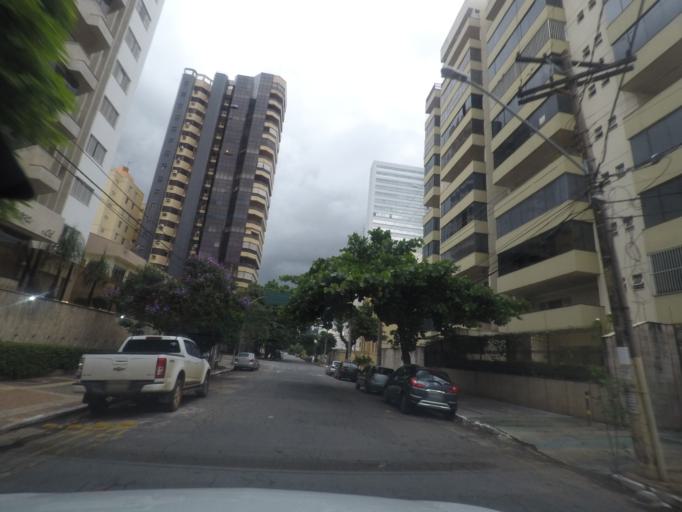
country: BR
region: Goias
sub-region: Goiania
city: Goiania
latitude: -16.6837
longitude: -49.2632
